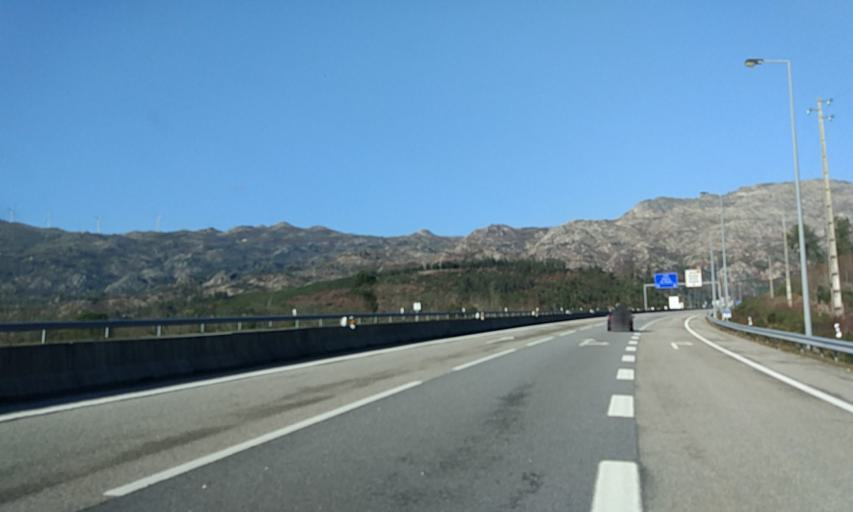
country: PT
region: Viseu
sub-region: Vouzela
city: Vouzela
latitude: 40.6506
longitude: -8.0646
